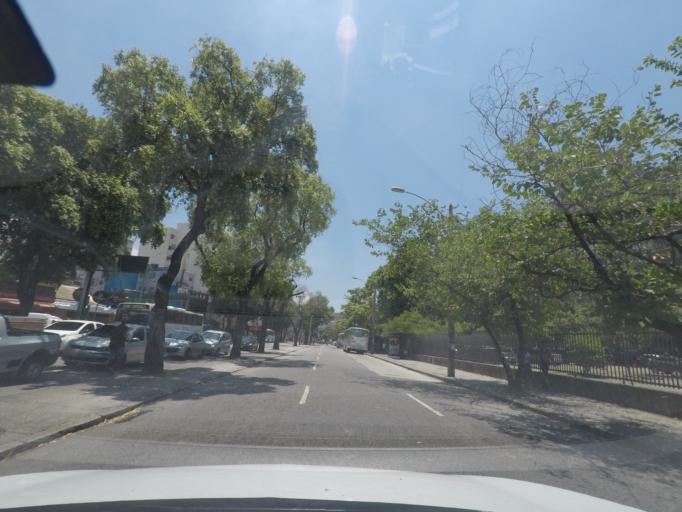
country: BR
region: Rio de Janeiro
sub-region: Rio De Janeiro
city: Rio de Janeiro
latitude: -22.9130
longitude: -43.2355
